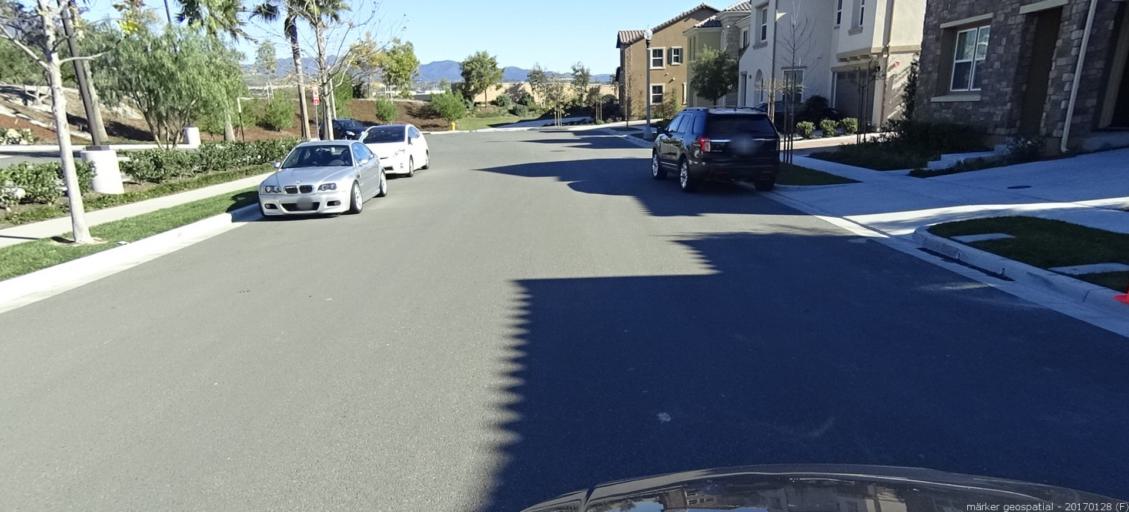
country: US
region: California
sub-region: Orange County
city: Foothill Ranch
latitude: 33.6722
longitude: -117.6737
